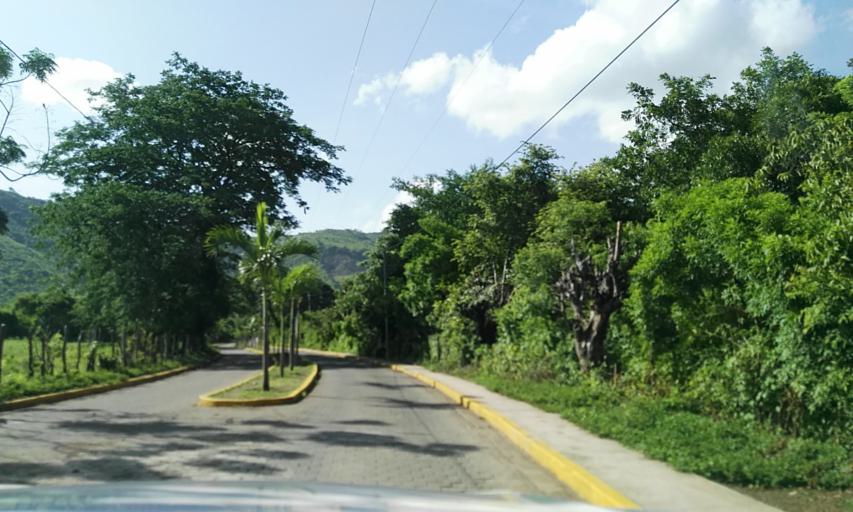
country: NI
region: Matagalpa
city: Terrabona
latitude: 12.7369
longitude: -85.9673
